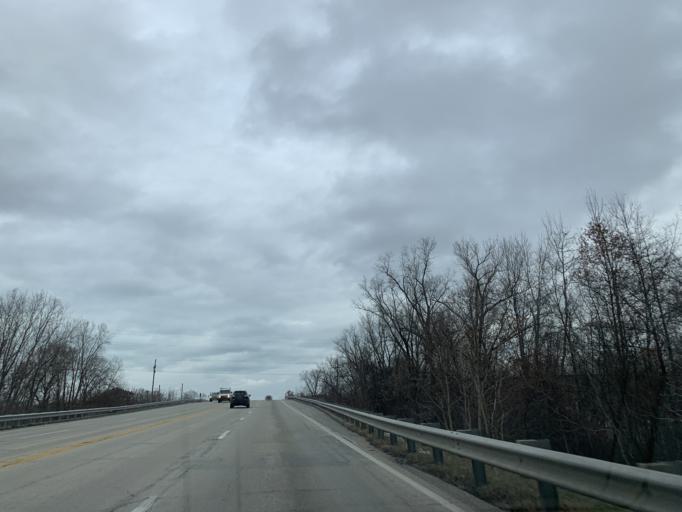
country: US
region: Indiana
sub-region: LaPorte County
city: Trail Creek
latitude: 41.7134
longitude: -86.8259
